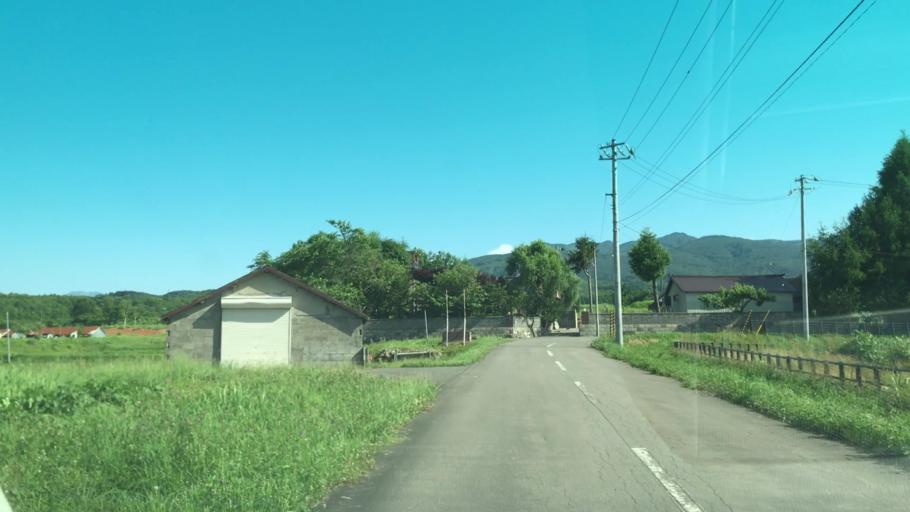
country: JP
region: Hokkaido
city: Iwanai
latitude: 42.9736
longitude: 140.6107
